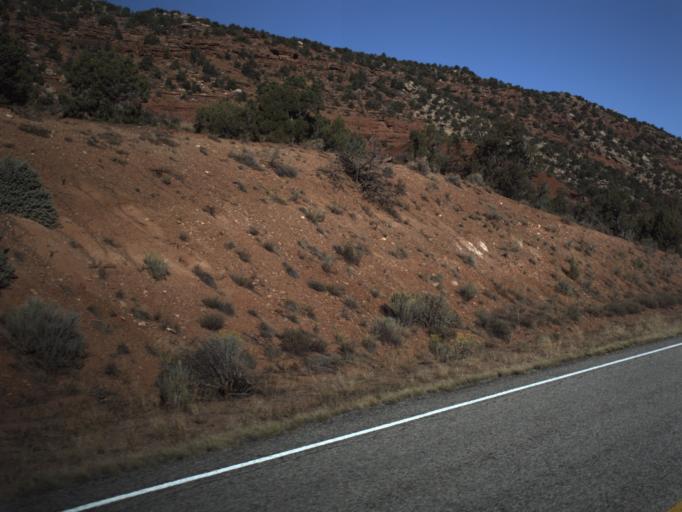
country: US
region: Utah
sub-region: San Juan County
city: Blanding
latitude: 37.5734
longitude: -110.0376
